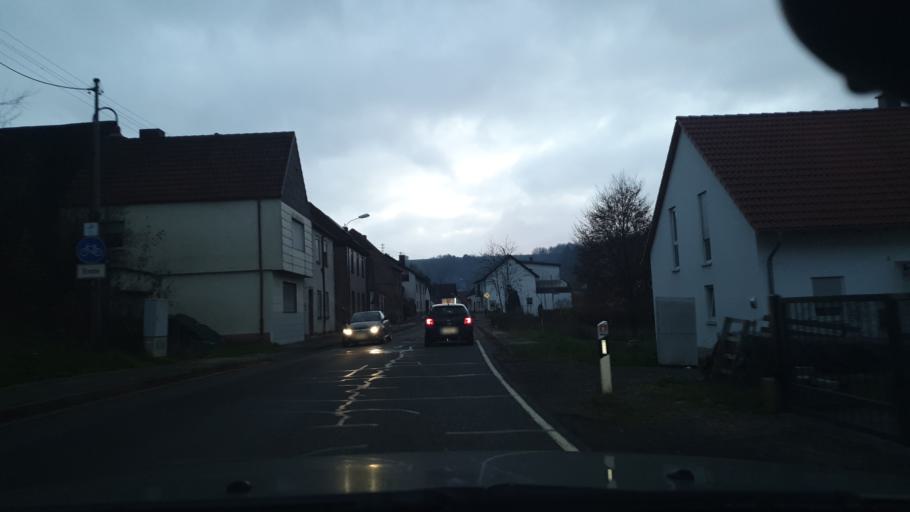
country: DE
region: Rheinland-Pfalz
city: Queidersbach
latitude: 49.3786
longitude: 7.6287
